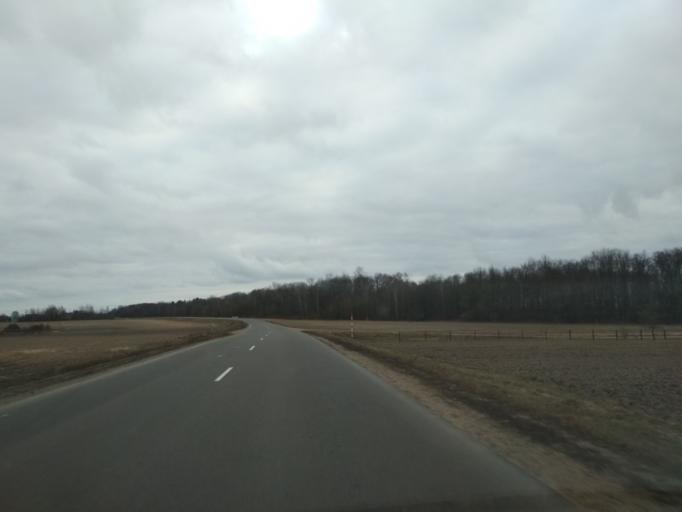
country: BY
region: Minsk
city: Druzhny
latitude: 53.5772
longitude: 27.9257
